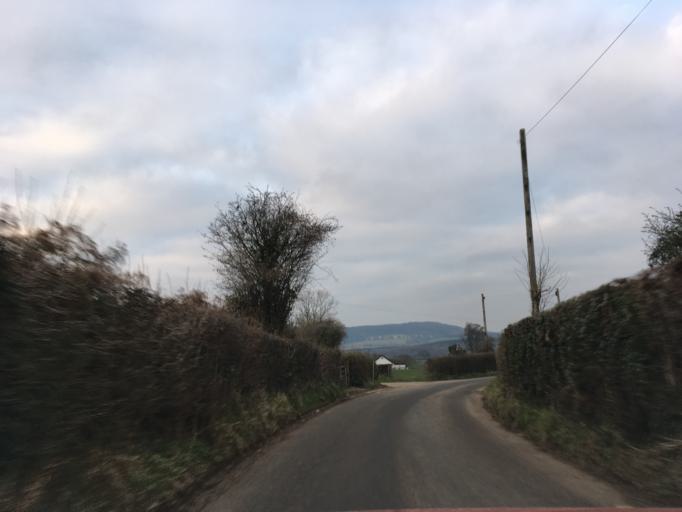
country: GB
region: Wales
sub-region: Newport
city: Marshfield
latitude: 51.5604
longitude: -3.0968
